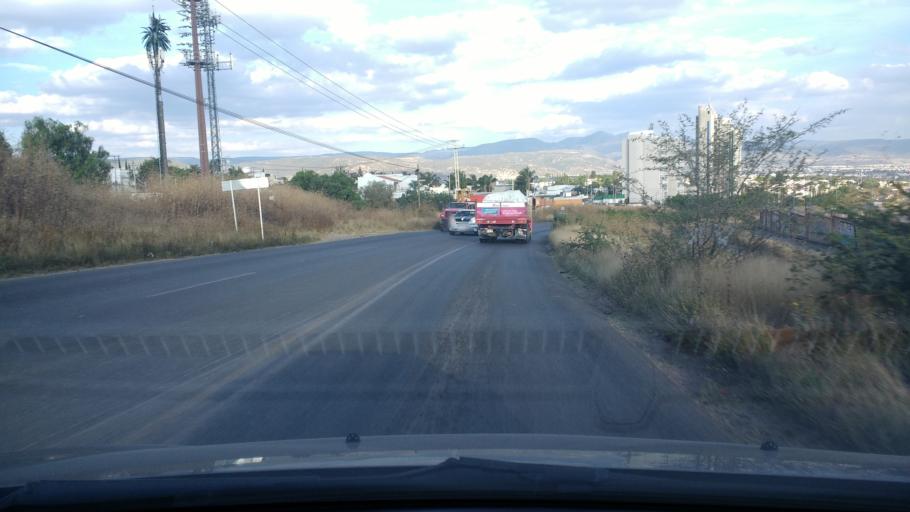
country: MX
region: Guanajuato
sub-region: Leon
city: La Ermita
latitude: 21.1746
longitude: -101.7145
